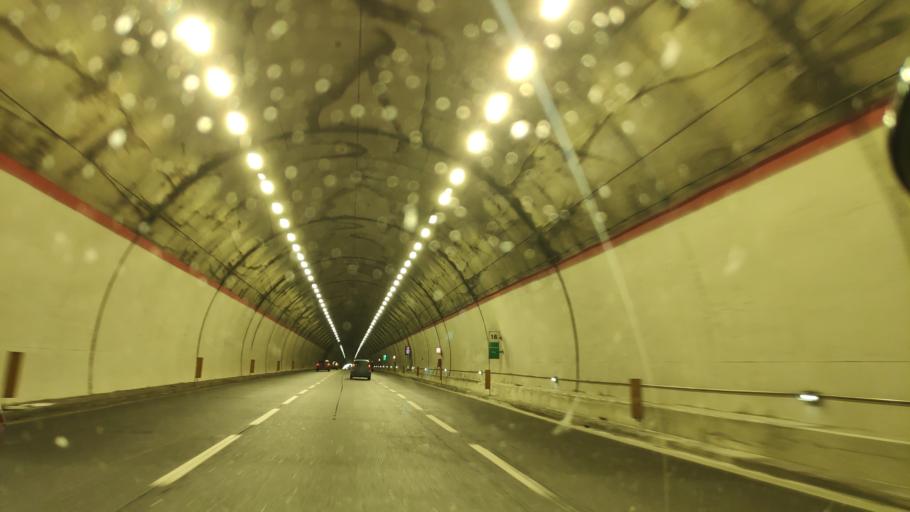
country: IT
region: Campania
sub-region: Provincia di Salerno
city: Pezzano-Filetta
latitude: 40.6761
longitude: 14.8574
